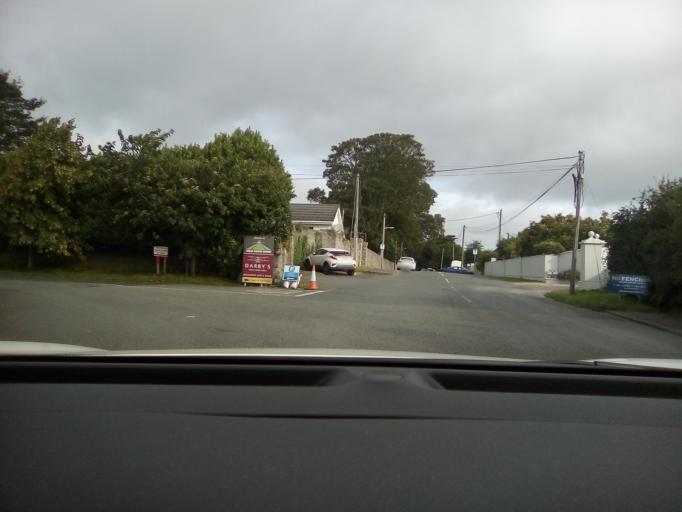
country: IE
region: Leinster
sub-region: Kildare
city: Leixlip
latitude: 53.3554
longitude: -6.4809
